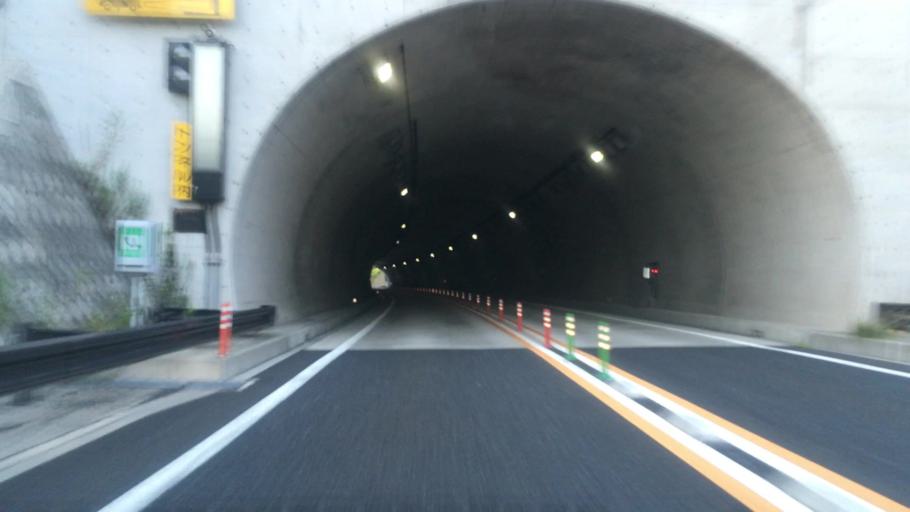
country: JP
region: Tottori
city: Tottori
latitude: 35.5550
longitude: 134.2809
